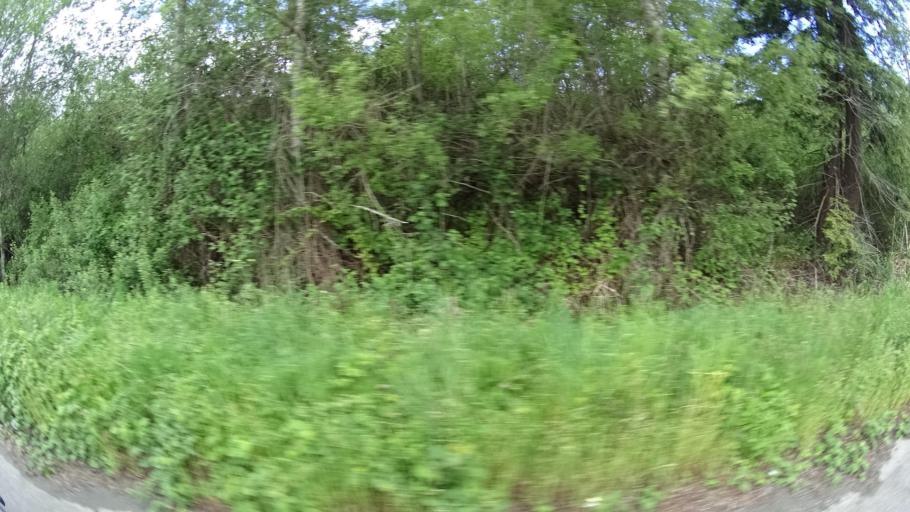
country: US
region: California
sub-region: Humboldt County
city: Blue Lake
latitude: 40.8990
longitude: -124.0096
